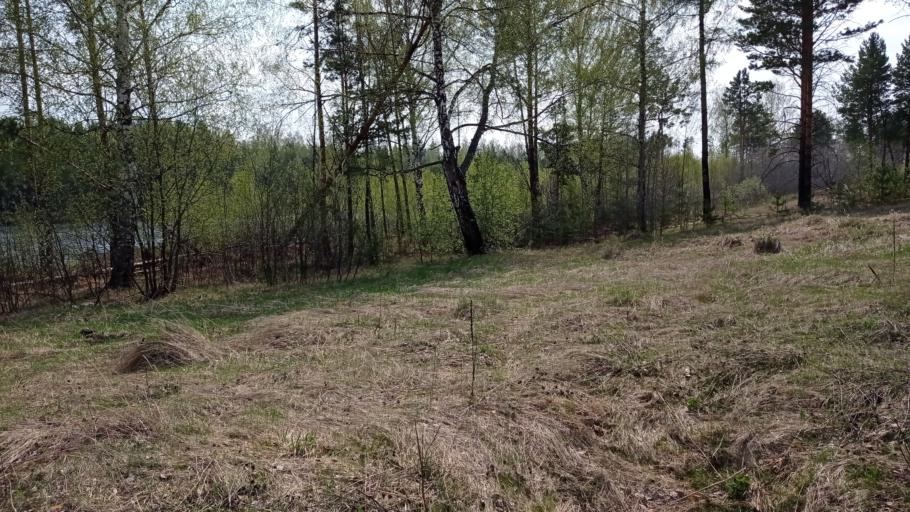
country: RU
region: Tomsk
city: Timiryazevskoye
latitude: 56.4195
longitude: 84.6237
